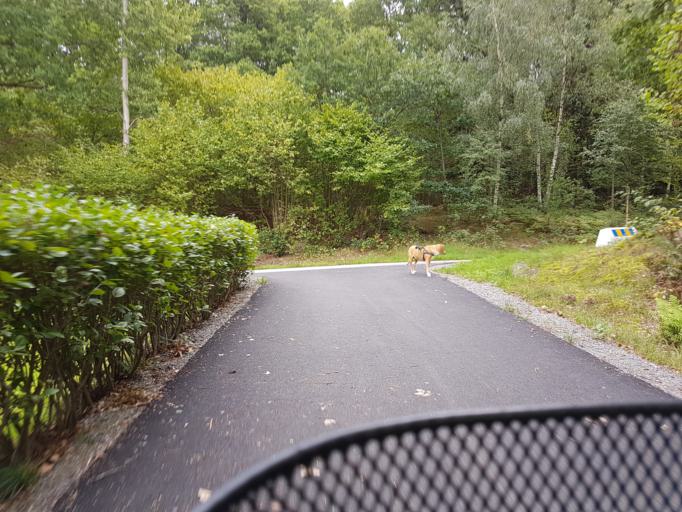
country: SE
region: Vaestra Goetaland
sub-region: Ale Kommun
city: Nodinge-Nol
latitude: 57.9032
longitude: 12.0595
